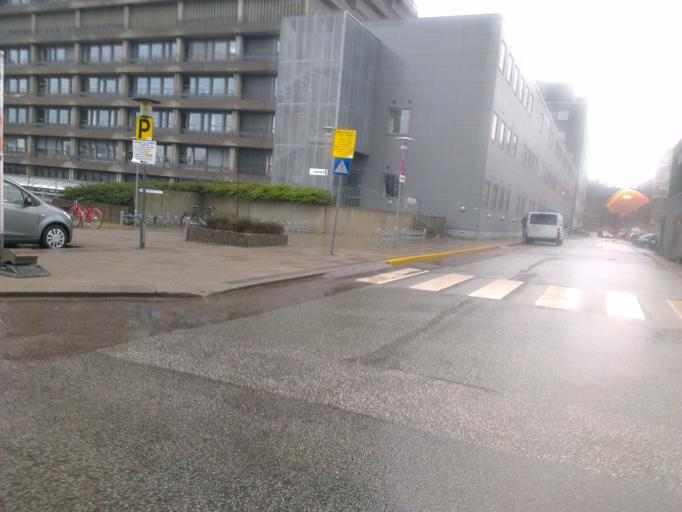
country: DK
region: Capital Region
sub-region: Kobenhavn
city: Copenhagen
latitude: 55.6979
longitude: 12.5662
